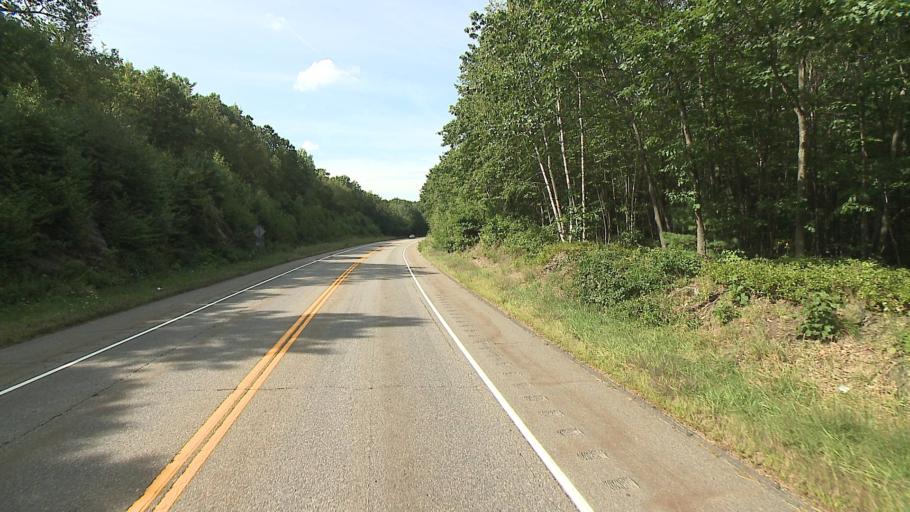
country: US
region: Connecticut
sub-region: Litchfield County
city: Litchfield
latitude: 41.7465
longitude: -73.1634
